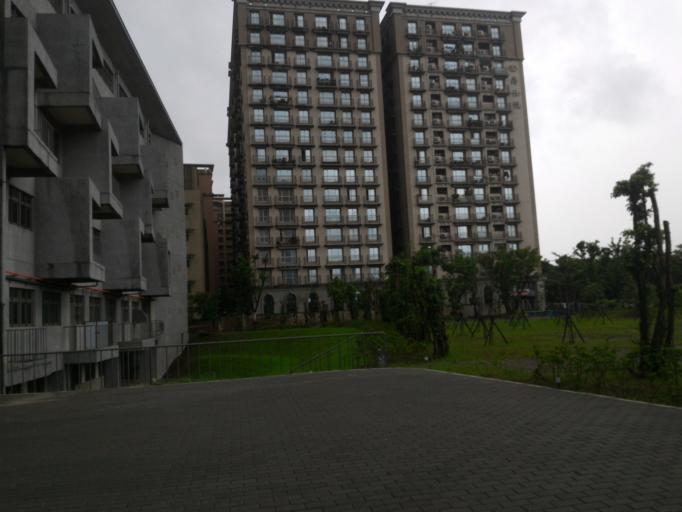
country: TW
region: Taiwan
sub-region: Taoyuan
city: Taoyuan
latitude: 24.9488
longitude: 121.3756
